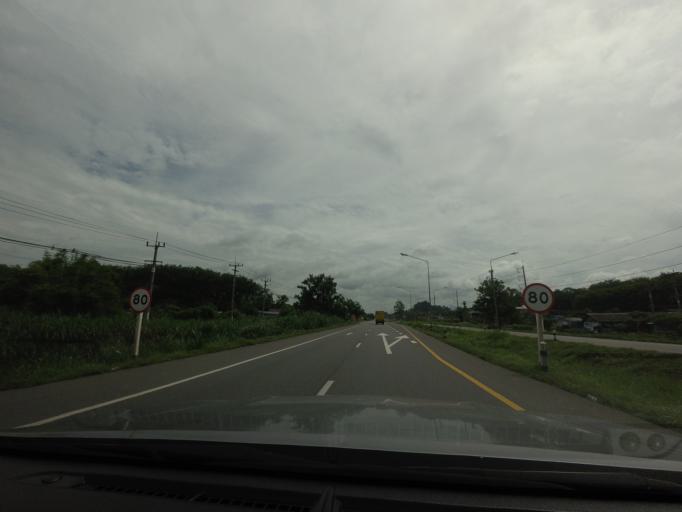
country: TH
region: Surat Thani
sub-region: Amphoe Wiang Sa
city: Wiang Sa
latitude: 8.5624
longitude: 99.3441
